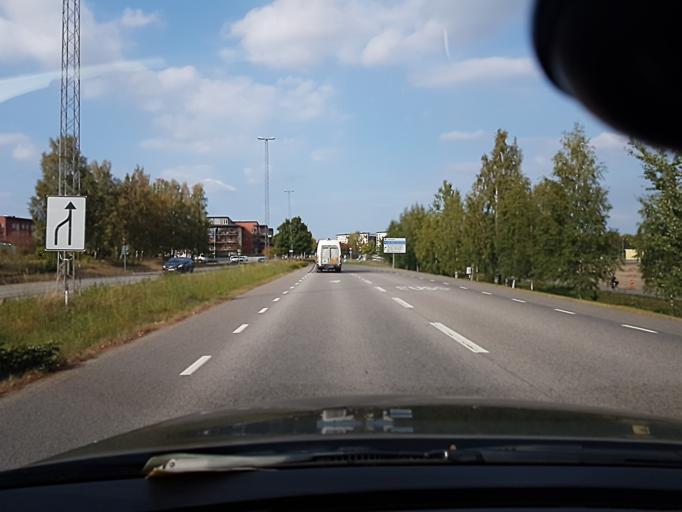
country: SE
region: Kronoberg
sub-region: Vaxjo Kommun
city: Vaexjoe
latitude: 56.8567
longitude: 14.8217
